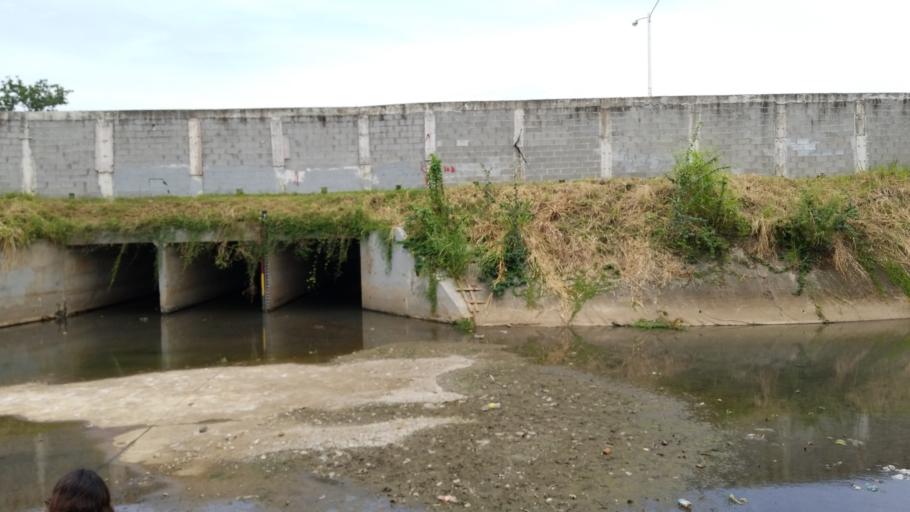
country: PA
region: Panama
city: San Miguelito
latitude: 9.0376
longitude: -79.4391
